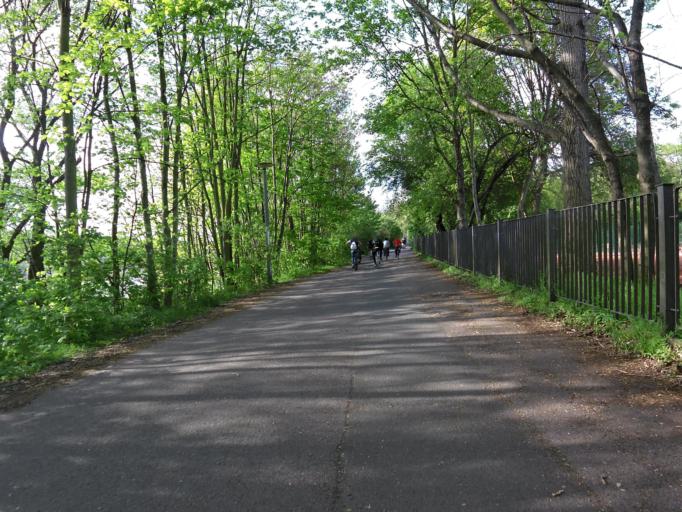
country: DE
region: Saxony
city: Leipzig
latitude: 51.3498
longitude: 12.3429
